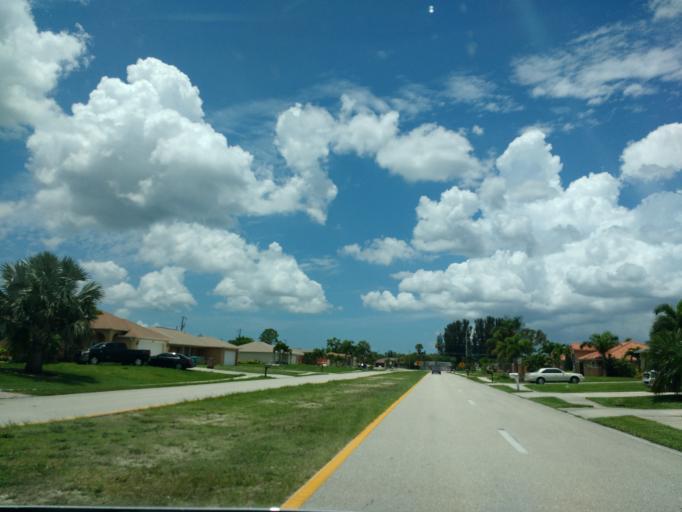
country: US
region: Florida
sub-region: Lee County
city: Cape Coral
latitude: 26.5838
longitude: -82.0147
